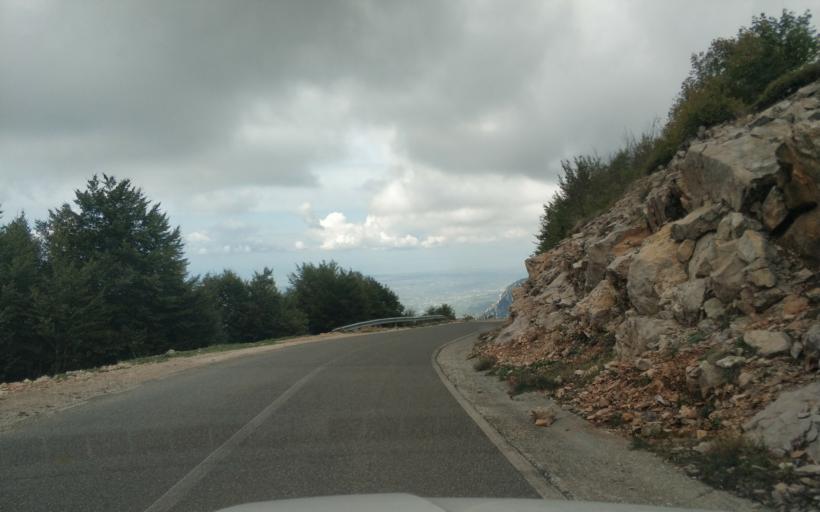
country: AL
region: Durres
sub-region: Rrethi i Krujes
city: Kruje
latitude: 41.5206
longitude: 19.8056
